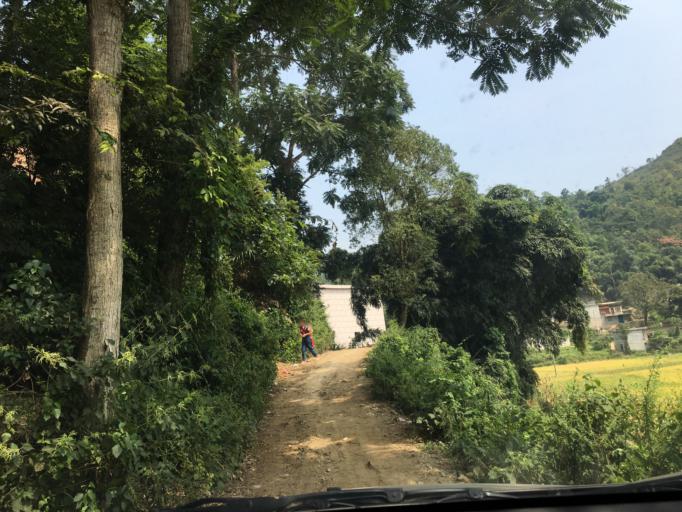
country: CN
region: Guizhou Sheng
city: Anshun
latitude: 25.5963
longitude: 105.6728
